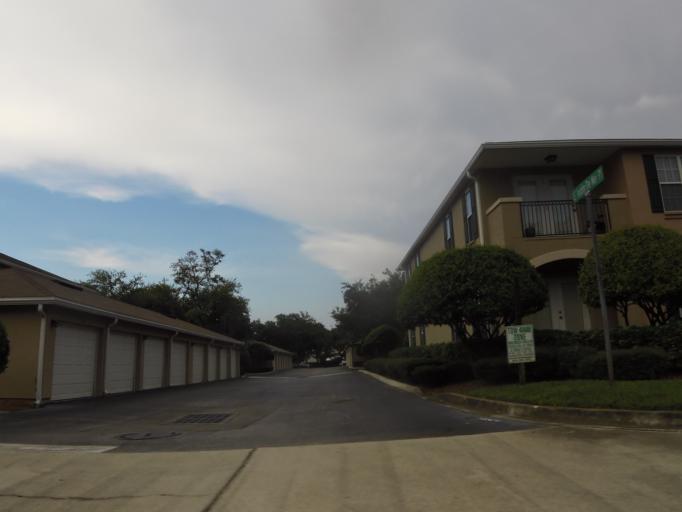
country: US
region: Florida
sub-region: Duval County
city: Jacksonville Beach
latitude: 30.2868
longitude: -81.4070
